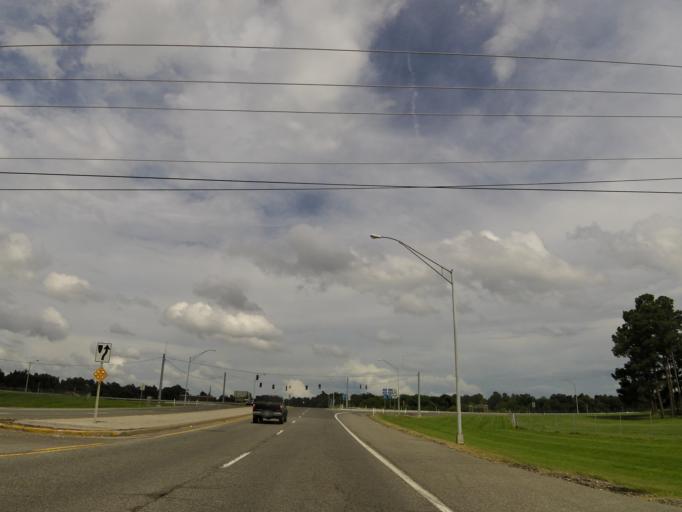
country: US
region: Kentucky
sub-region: McCracken County
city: Hendron
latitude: 37.0566
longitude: -88.6575
